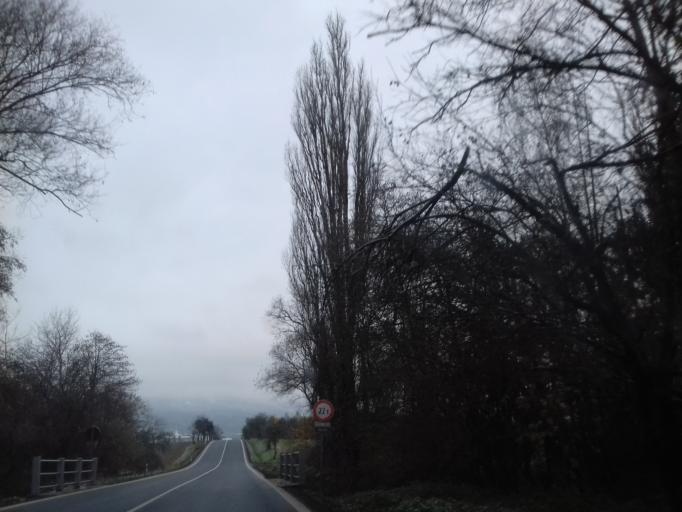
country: CZ
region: Plzensky
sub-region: Okres Domazlice
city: Klenci pod Cerchovem
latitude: 49.4418
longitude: 12.8405
